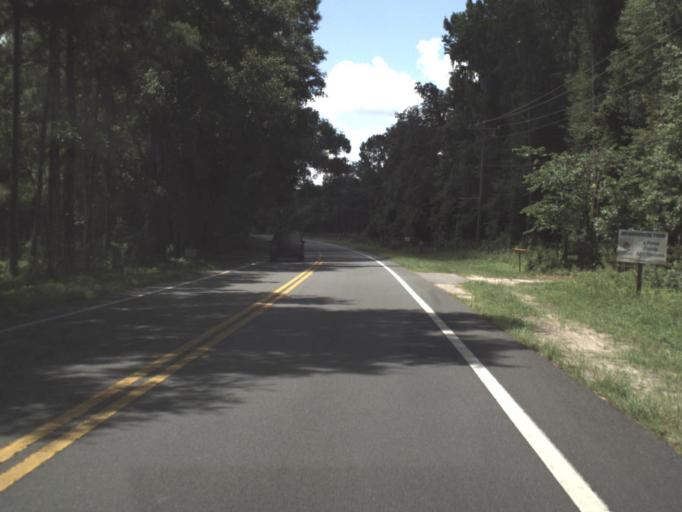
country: US
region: Florida
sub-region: Clay County
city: Keystone Heights
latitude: 29.7012
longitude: -82.0422
